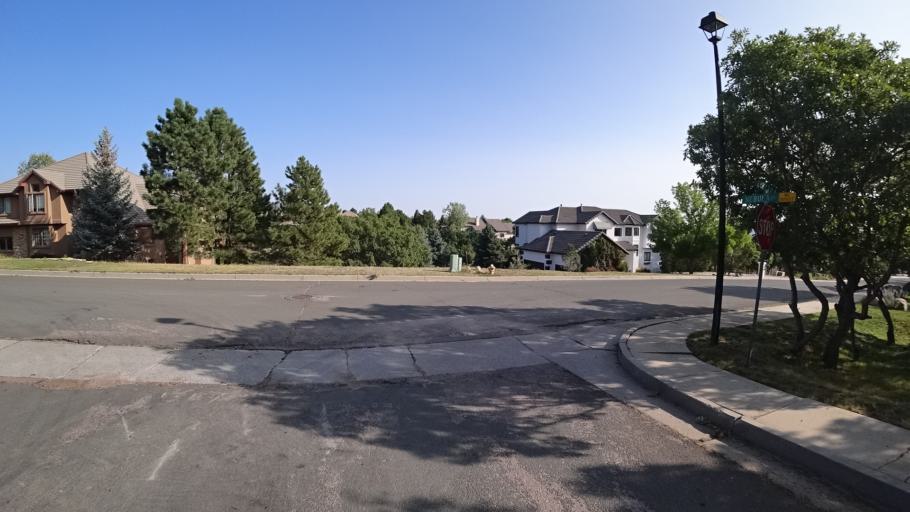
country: US
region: Colorado
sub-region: El Paso County
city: Manitou Springs
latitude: 38.8225
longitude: -104.8804
